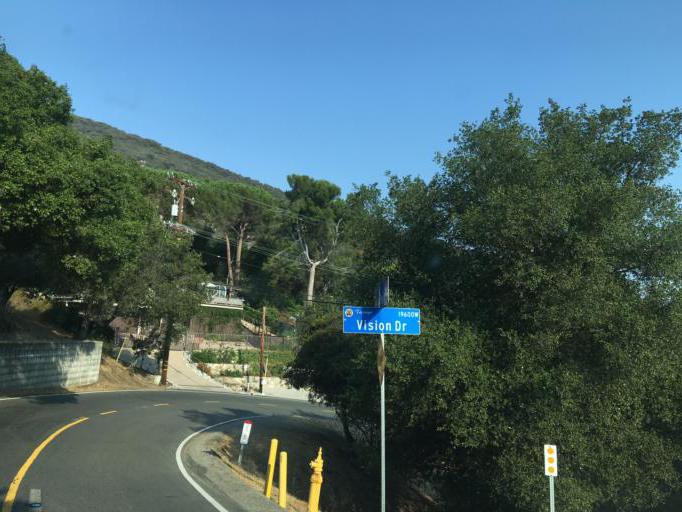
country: US
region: California
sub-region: Los Angeles County
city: Topanga
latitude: 34.0788
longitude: -118.6027
